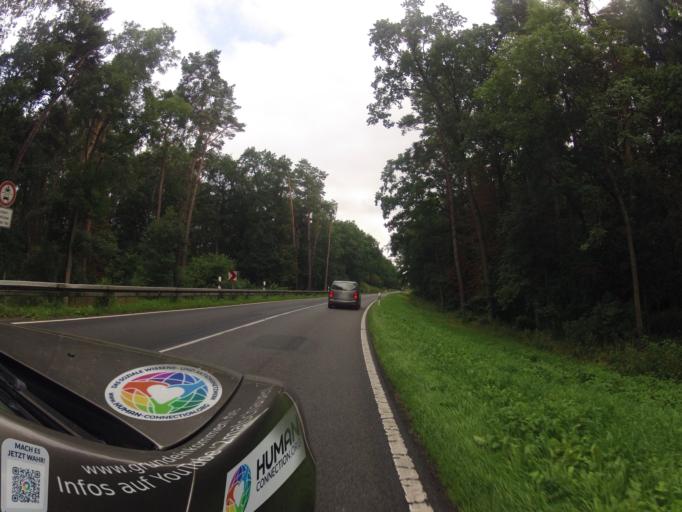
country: DE
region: Mecklenburg-Vorpommern
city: Lassan
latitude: 53.8836
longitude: 13.7910
